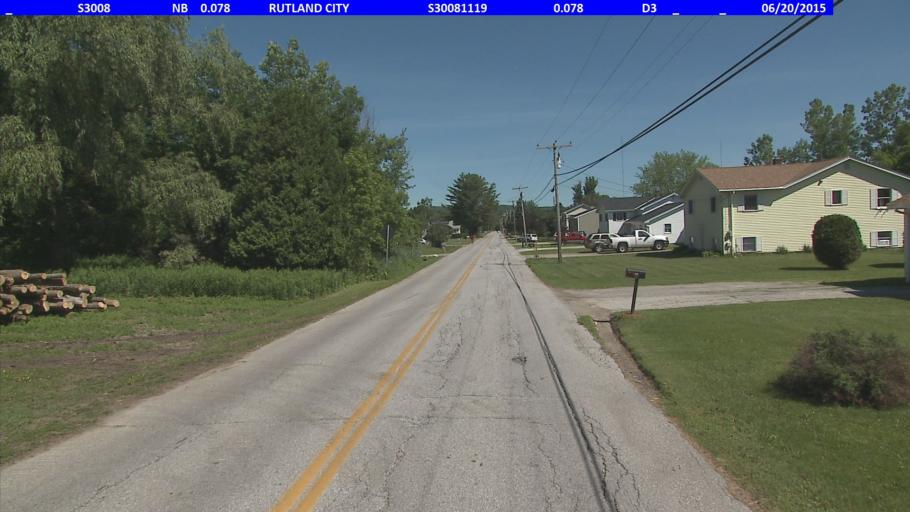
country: US
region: Vermont
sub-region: Rutland County
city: Rutland
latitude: 43.5878
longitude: -72.9907
